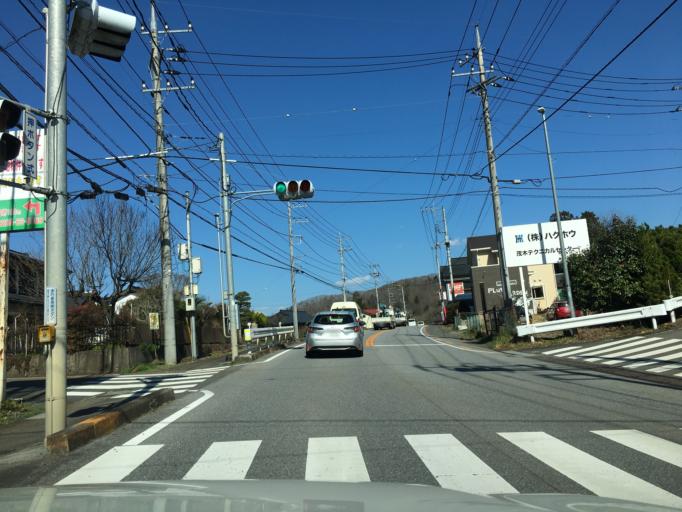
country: JP
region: Tochigi
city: Motegi
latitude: 36.5428
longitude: 140.2169
